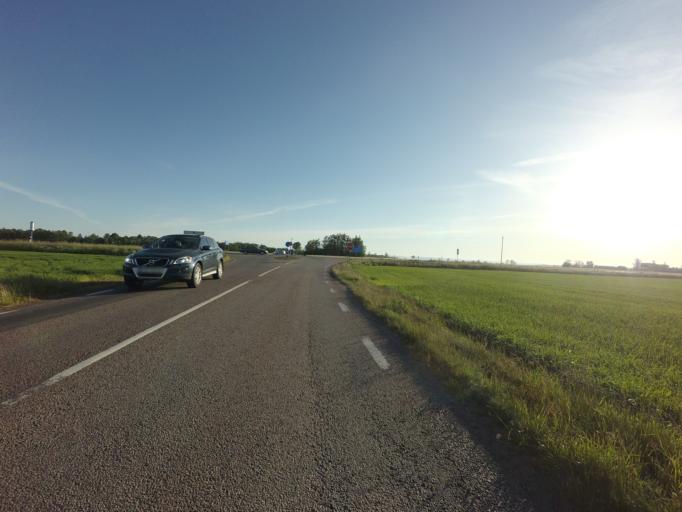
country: SE
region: Skane
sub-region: Hoganas Kommun
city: Hoganas
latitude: 56.2148
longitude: 12.6787
